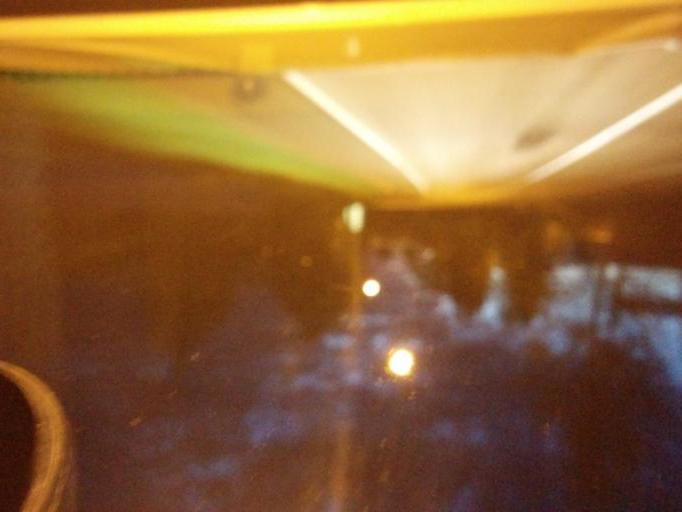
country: RU
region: Leningrad
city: Verkhniye Osel'ki
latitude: 60.2522
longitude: 30.4488
